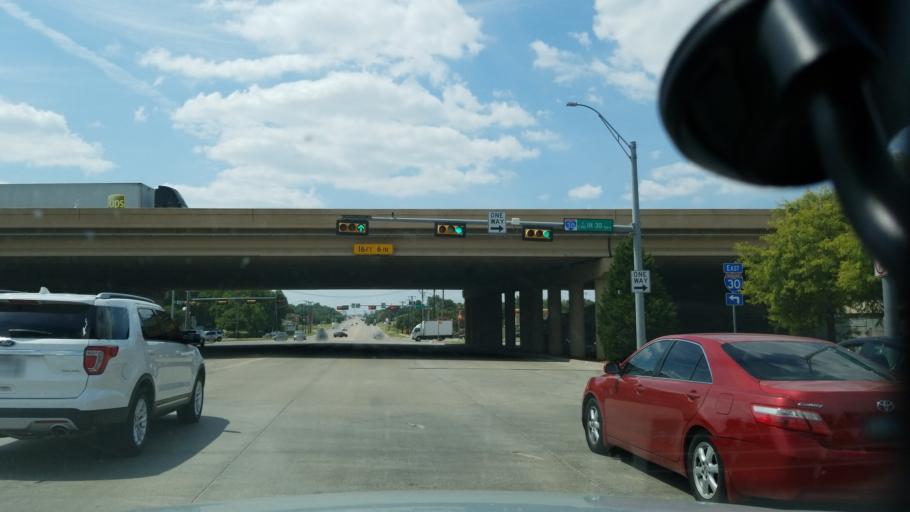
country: US
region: Texas
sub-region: Dallas County
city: Grand Prairie
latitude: 32.7592
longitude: -96.9950
